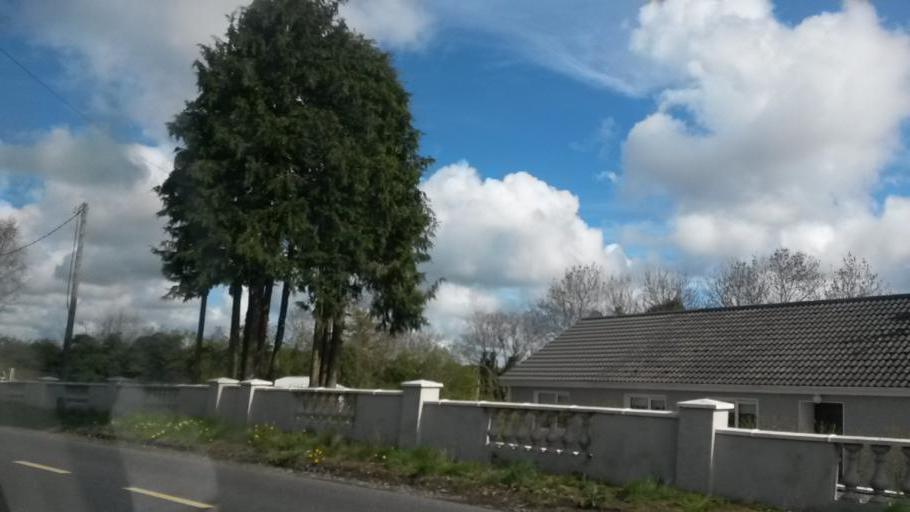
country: IE
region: Ulster
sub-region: An Cabhan
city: Ballyjamesduff
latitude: 53.8974
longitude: -7.1680
